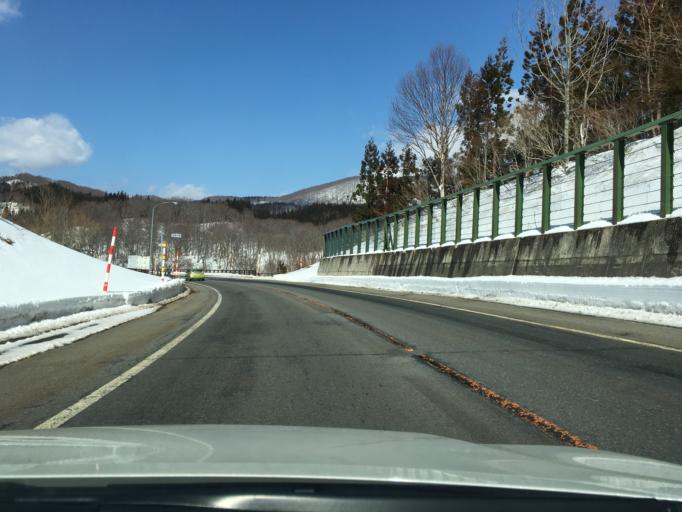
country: JP
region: Yamagata
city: Tsuruoka
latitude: 38.5765
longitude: 139.9433
